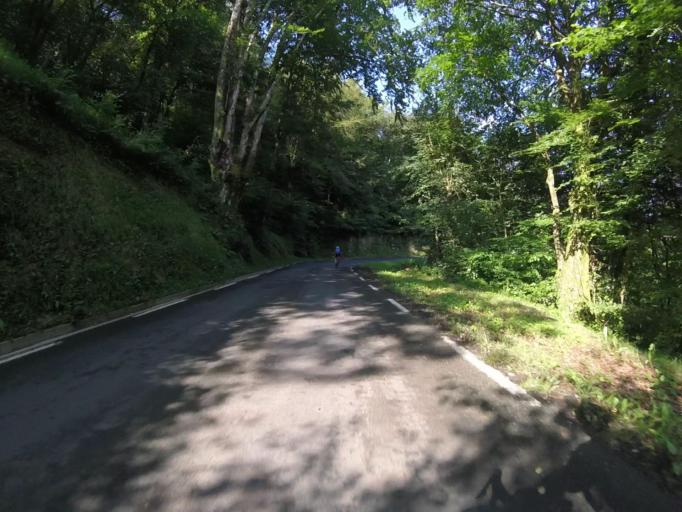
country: ES
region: Basque Country
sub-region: Provincia de Guipuzcoa
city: Larraul
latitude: 43.1787
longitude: -2.0930
